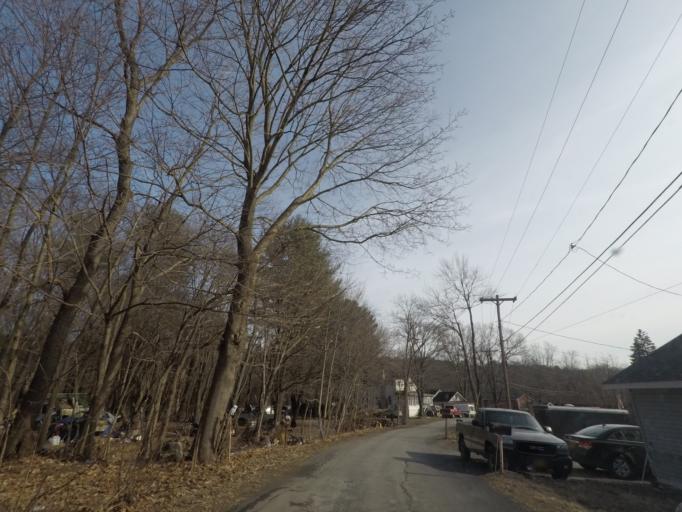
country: US
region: New York
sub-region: Rensselaer County
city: Nassau
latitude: 42.5443
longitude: -73.5995
